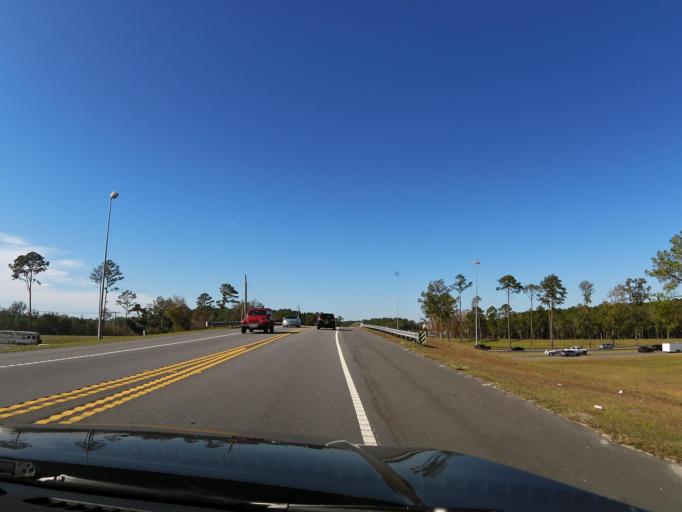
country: US
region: Georgia
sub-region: Liberty County
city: Midway
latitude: 31.7779
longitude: -81.3774
